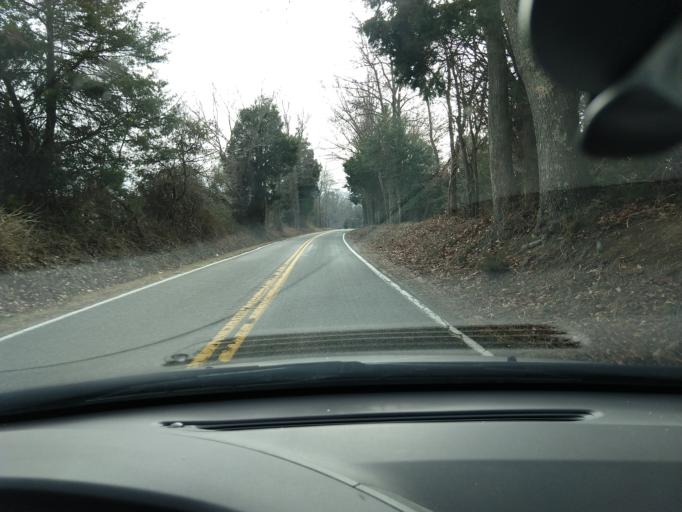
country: US
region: Virginia
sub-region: Henrico County
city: Fort Lee
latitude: 37.4391
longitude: -77.2350
